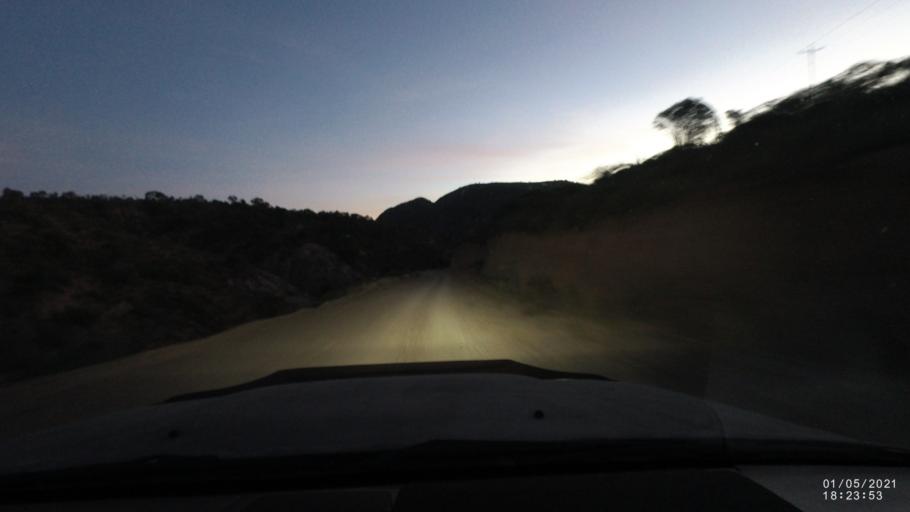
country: BO
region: Cochabamba
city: Capinota
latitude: -17.6594
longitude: -66.2413
